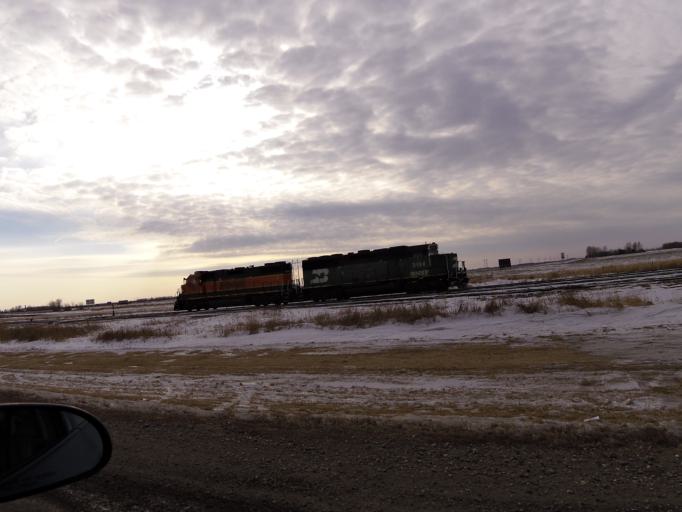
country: US
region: North Dakota
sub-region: Walsh County
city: Grafton
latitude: 48.5862
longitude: -97.1789
